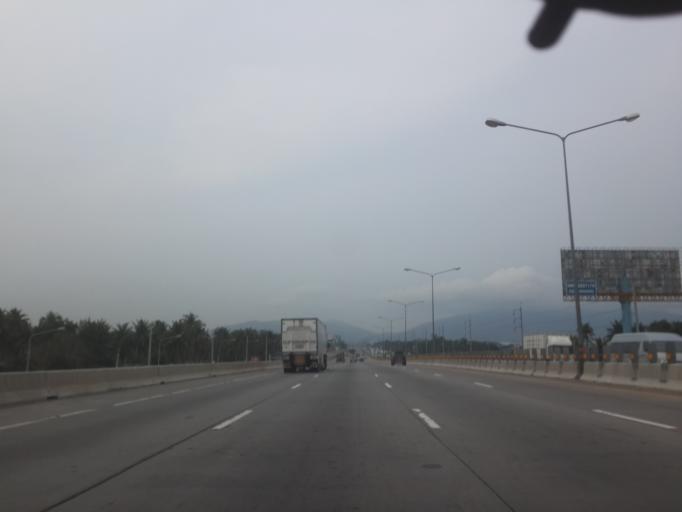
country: TH
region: Chon Buri
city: Si Racha
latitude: 13.1817
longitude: 100.9956
